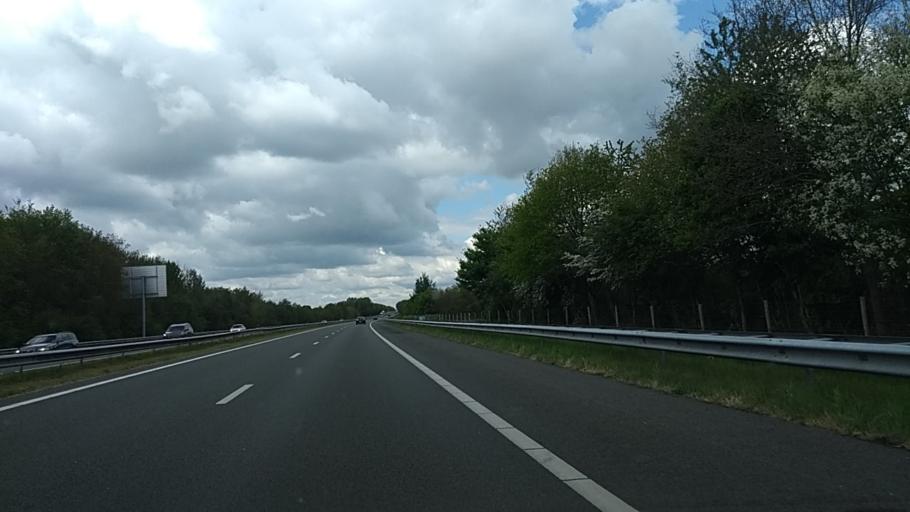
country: NL
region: Overijssel
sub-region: Gemeente Steenwijkerland
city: Steenwijkerwold
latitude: 52.8175
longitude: 6.0758
